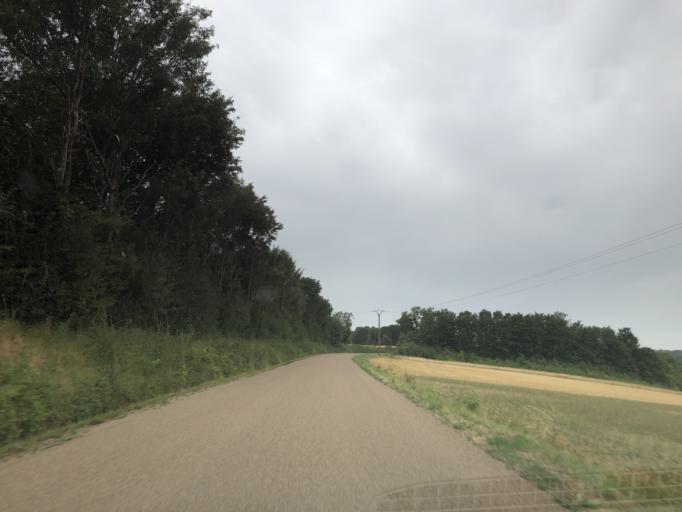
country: FR
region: Bourgogne
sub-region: Departement de l'Yonne
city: Charny
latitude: 47.9490
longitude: 3.1341
